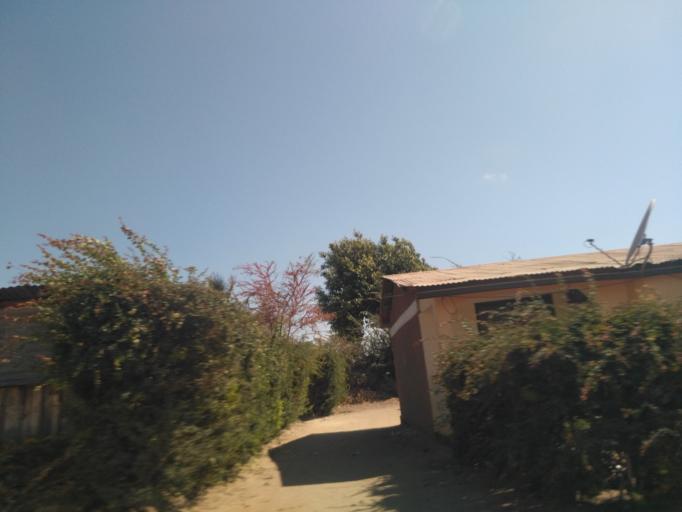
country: TZ
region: Dodoma
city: Dodoma
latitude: -6.1673
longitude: 35.7488
